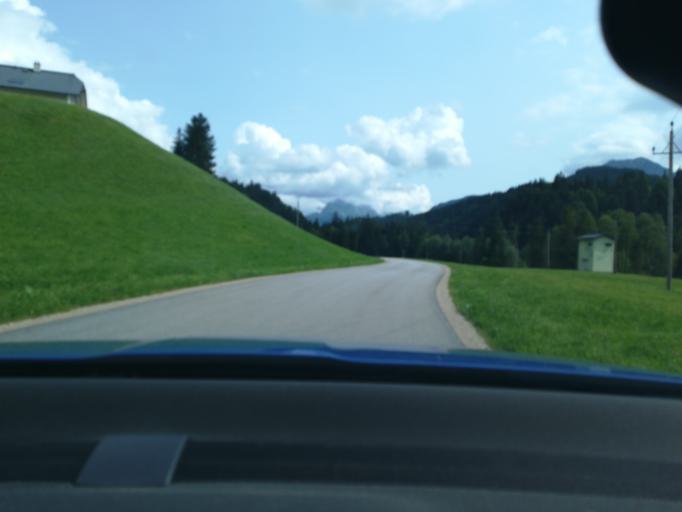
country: AT
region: Salzburg
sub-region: Politischer Bezirk Hallein
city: Abtenau
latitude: 47.5875
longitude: 13.3458
